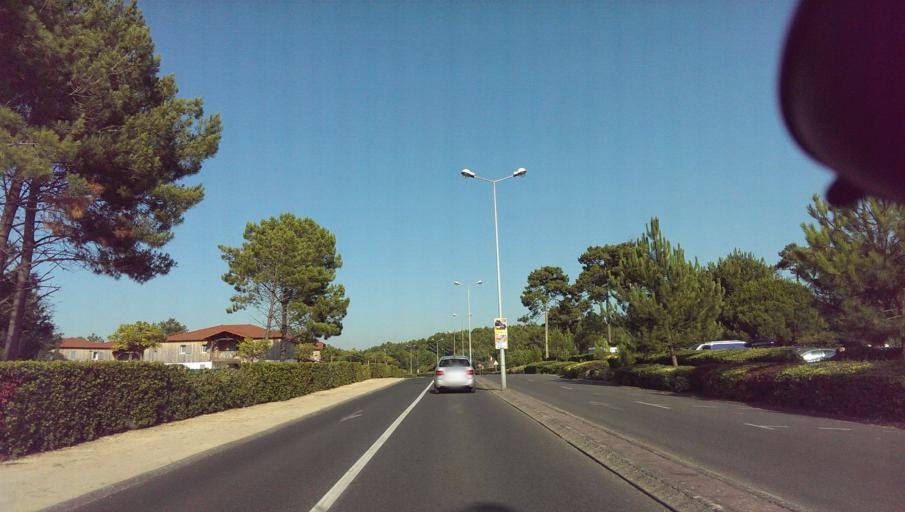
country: FR
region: Aquitaine
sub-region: Departement des Landes
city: Mimizan
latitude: 44.2116
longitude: -1.2861
